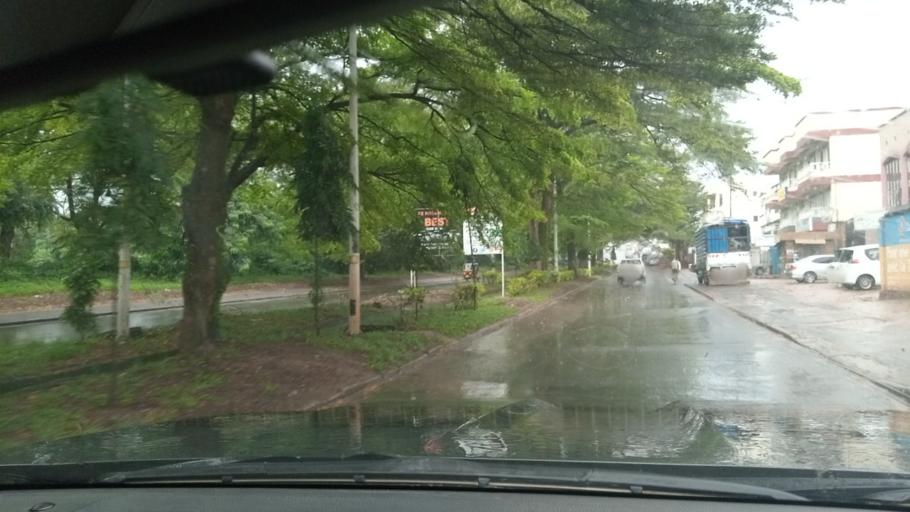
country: BI
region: Bujumbura Mairie
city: Bujumbura
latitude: -3.3804
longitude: 29.3570
